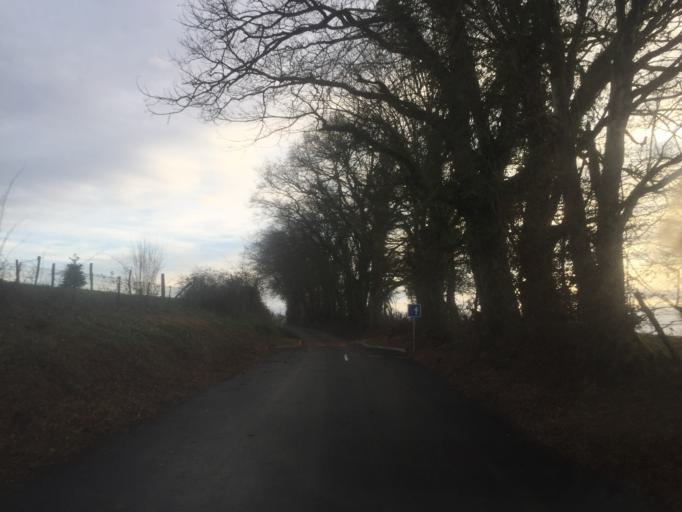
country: FR
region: Franche-Comte
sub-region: Departement du Jura
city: Orchamps
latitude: 47.1303
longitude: 5.6753
